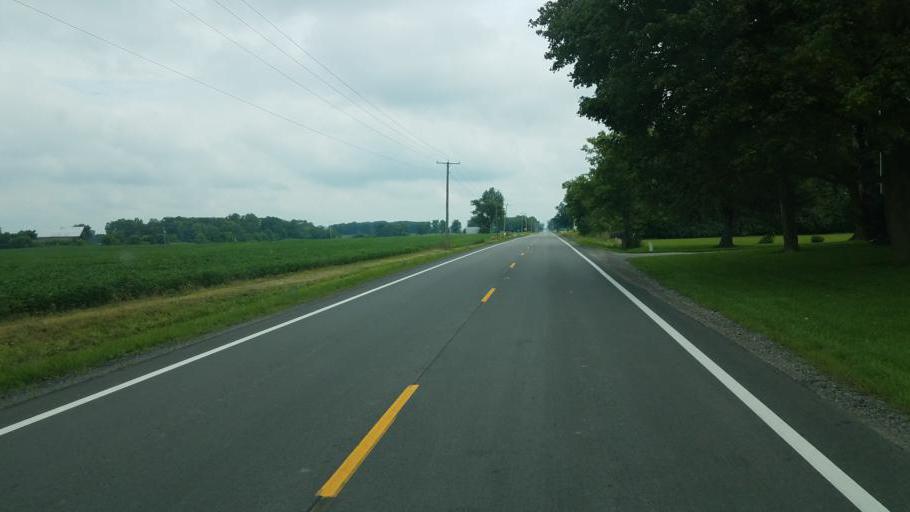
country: US
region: Ohio
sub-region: Marion County
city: Marion
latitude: 40.6270
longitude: -83.0266
